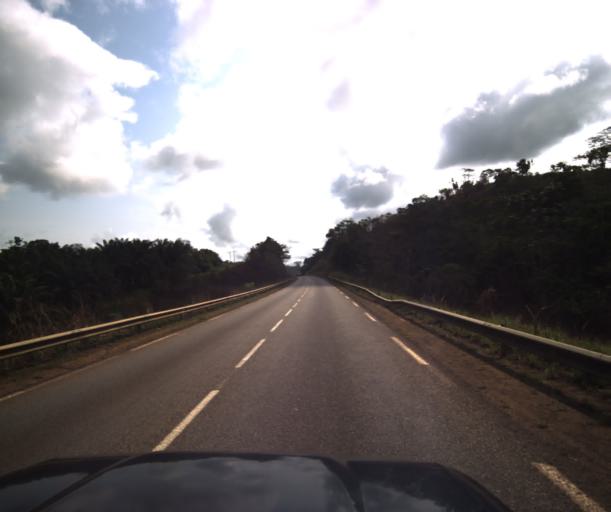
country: CM
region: Littoral
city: Edea
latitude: 3.7986
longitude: 10.2208
